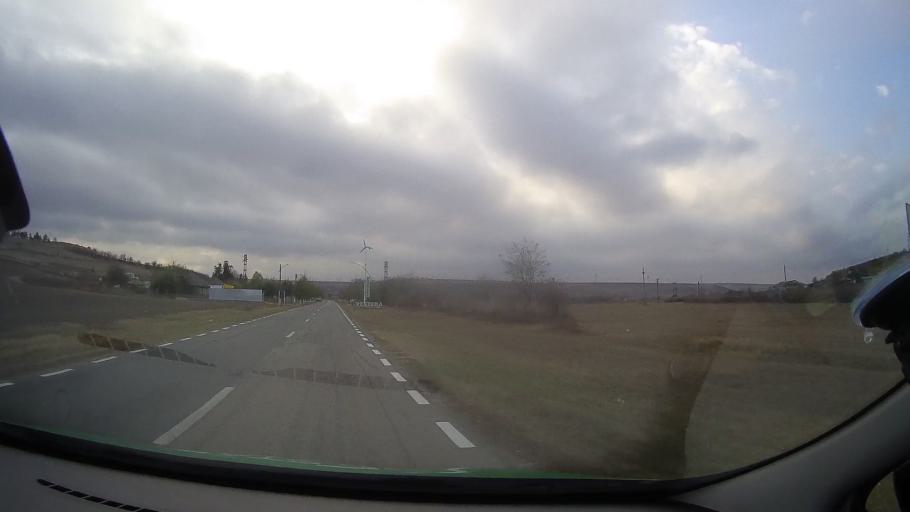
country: RO
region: Constanta
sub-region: Comuna Pestera
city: Pestera
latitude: 44.1955
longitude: 28.1291
